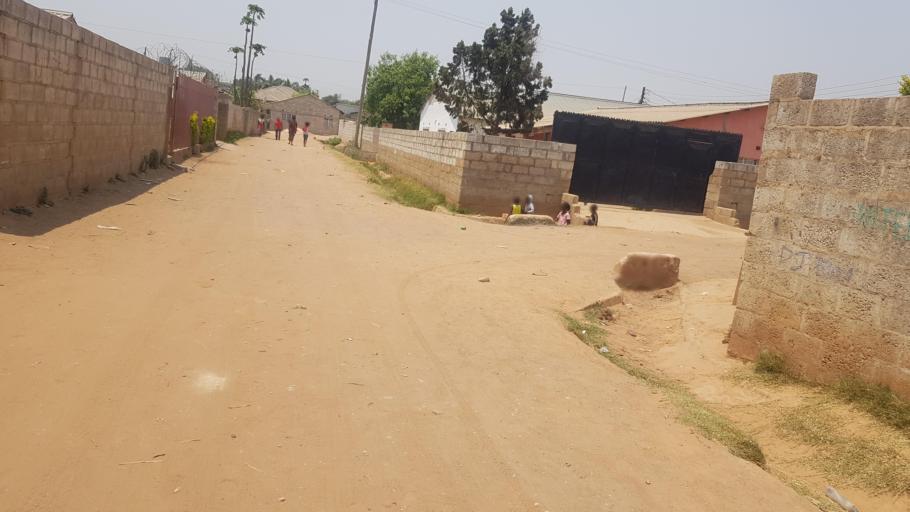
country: ZM
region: Lusaka
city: Lusaka
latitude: -15.4364
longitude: 28.3793
